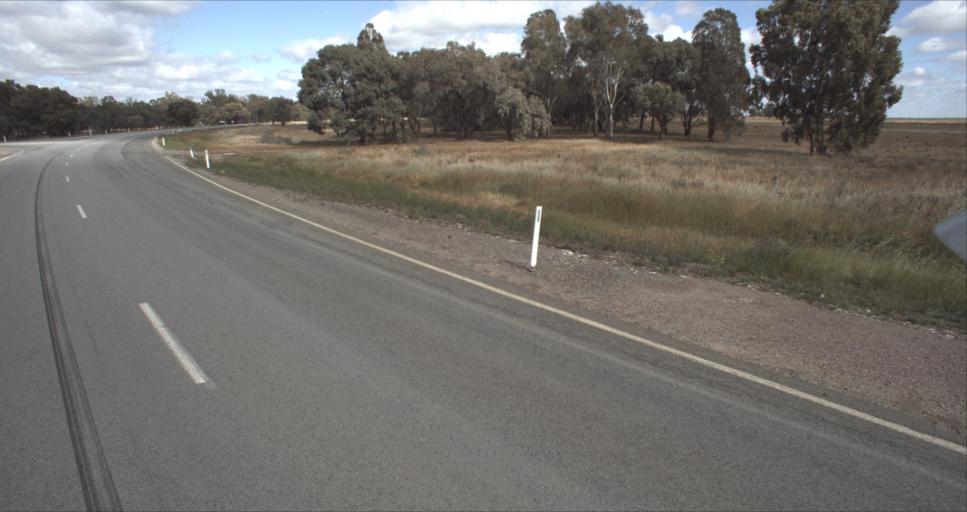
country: AU
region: New South Wales
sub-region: Murrumbidgee Shire
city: Darlington Point
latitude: -34.5974
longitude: 146.1609
